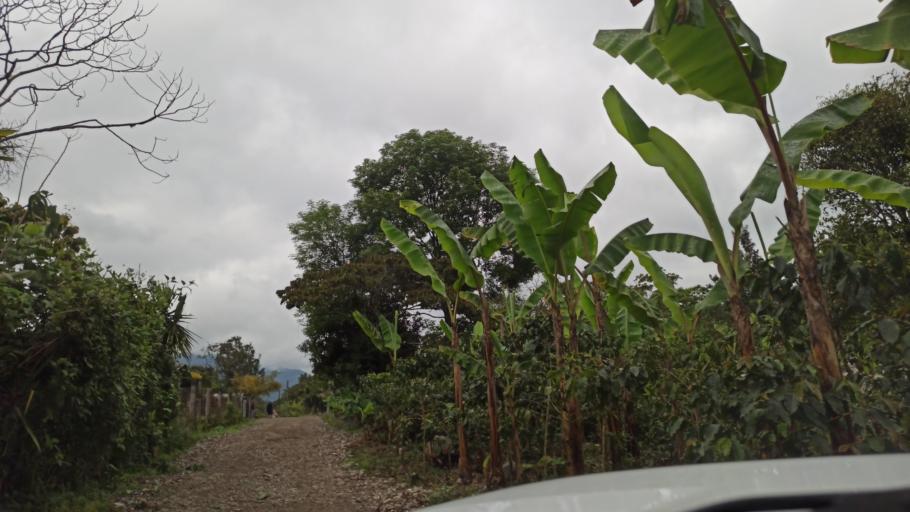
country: MX
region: Veracruz
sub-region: Chocaman
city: San Jose Neria
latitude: 18.9940
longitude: -97.0018
